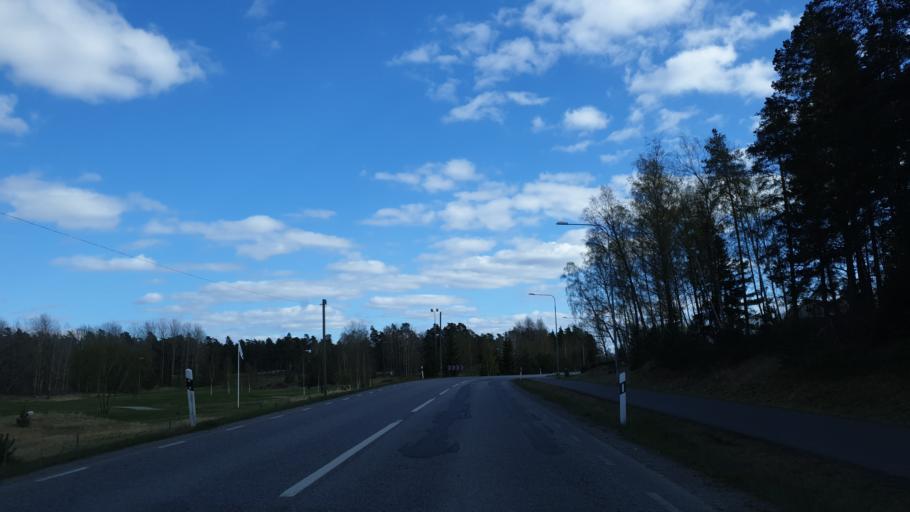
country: SE
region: Stockholm
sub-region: Sigtuna Kommun
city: Rosersberg
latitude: 59.6067
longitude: 17.8799
